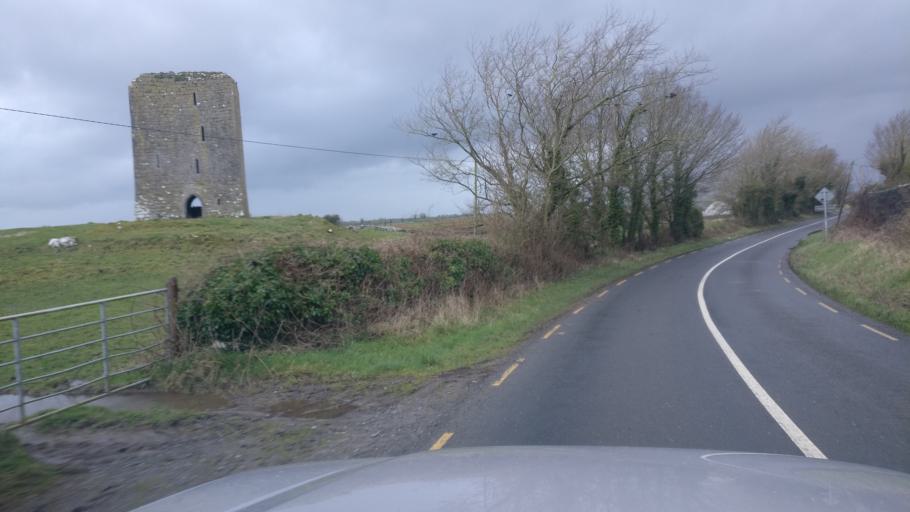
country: IE
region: Connaught
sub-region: County Galway
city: Loughrea
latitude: 53.1675
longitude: -8.6783
